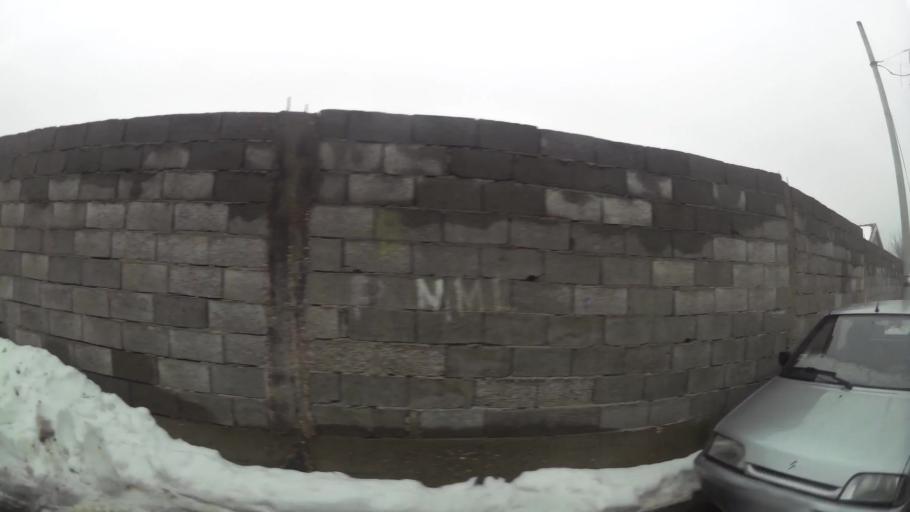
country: RS
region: Central Serbia
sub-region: Belgrade
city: Zvezdara
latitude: 44.7805
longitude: 20.5294
